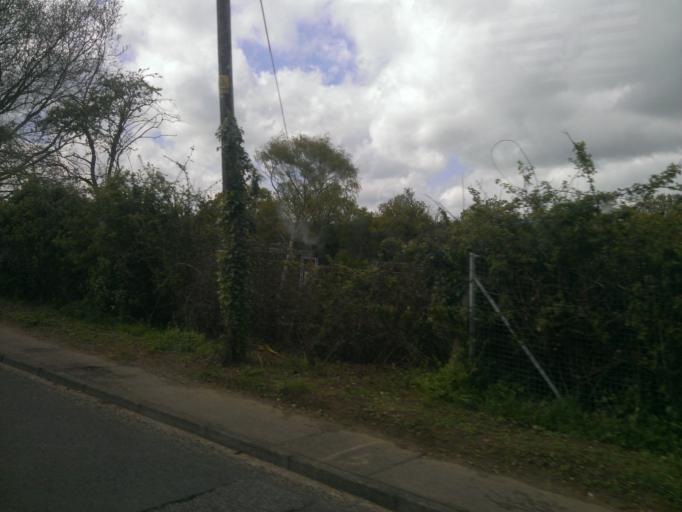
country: GB
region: England
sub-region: Essex
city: Eight Ash Green
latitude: 51.8930
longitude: 0.8331
